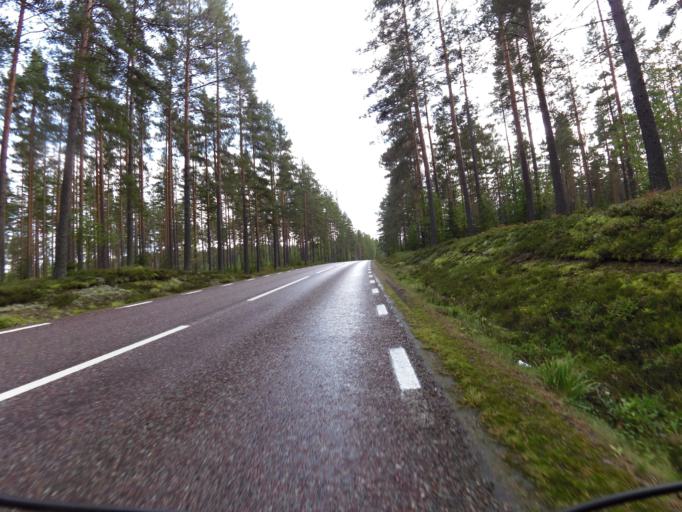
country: SE
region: Gaevleborg
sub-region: Ockelbo Kommun
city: Ockelbo
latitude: 60.8151
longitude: 16.7048
